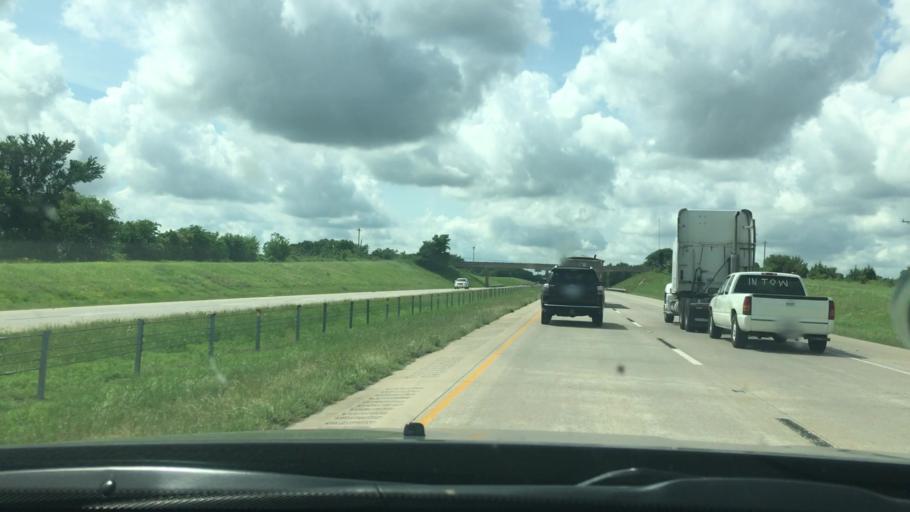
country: US
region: Oklahoma
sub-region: Love County
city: Marietta
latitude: 33.8557
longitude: -97.1343
